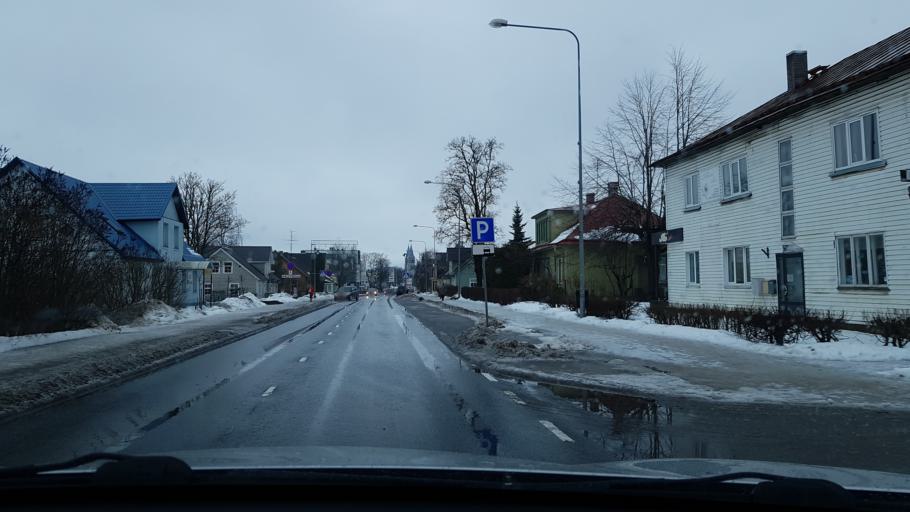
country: EE
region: Raplamaa
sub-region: Rapla vald
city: Rapla
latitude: 59.0013
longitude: 24.7927
